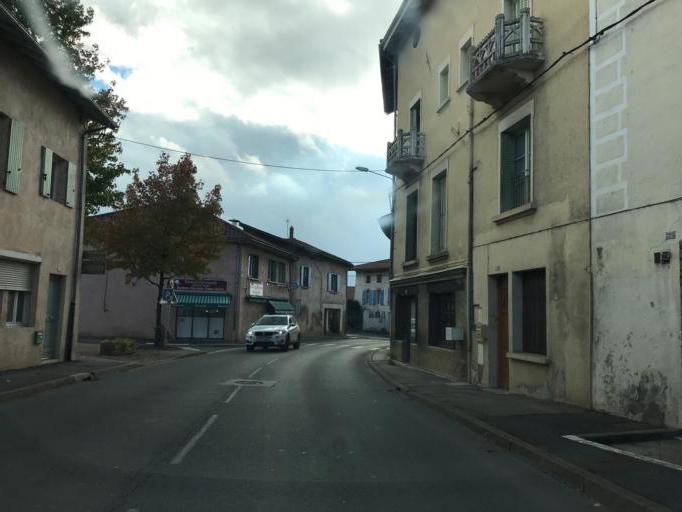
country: FR
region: Rhone-Alpes
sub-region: Departement de l'Ain
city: Neuville-les-Dames
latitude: 46.1624
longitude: 5.0039
